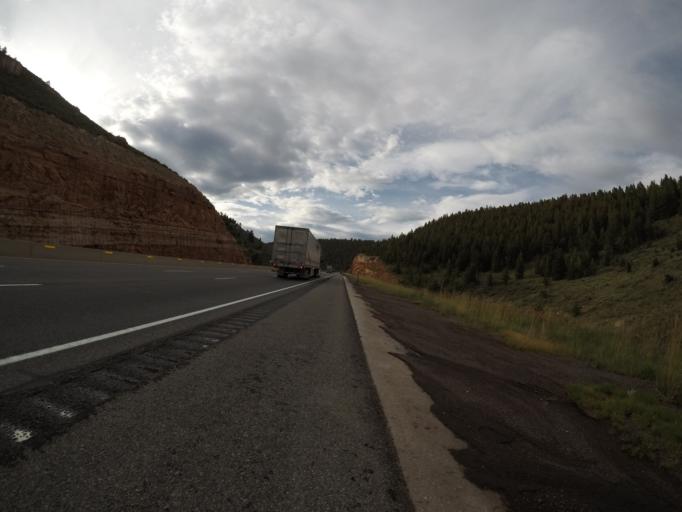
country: US
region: Wyoming
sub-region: Albany County
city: Laramie
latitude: 41.2697
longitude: -105.4799
